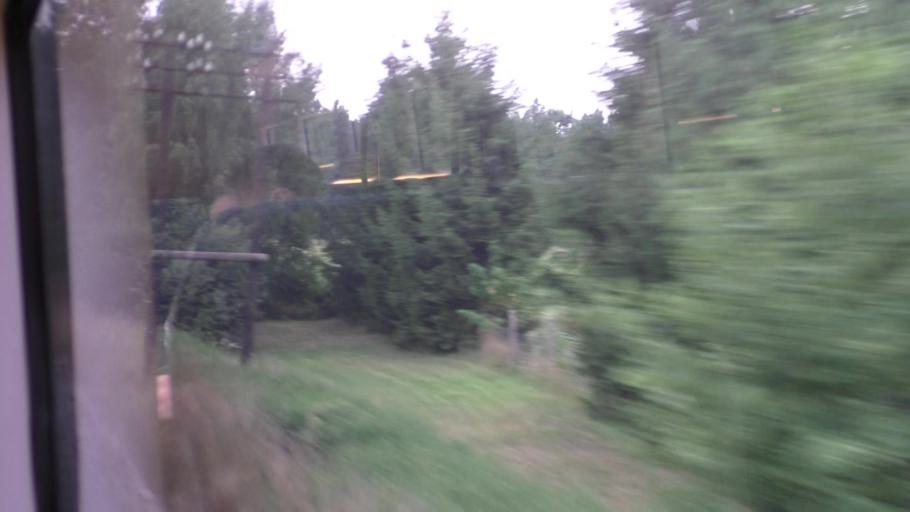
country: DE
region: Saxony
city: Horka
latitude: 51.2783
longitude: 14.9033
